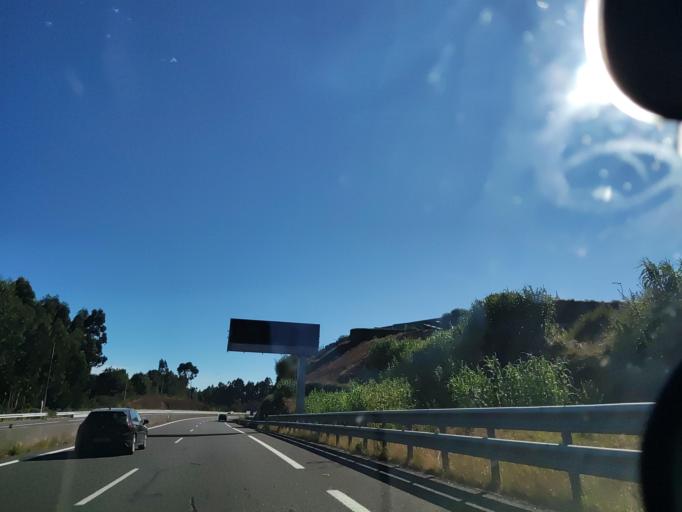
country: ES
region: Galicia
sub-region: Provincia da Coruna
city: Boiro
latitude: 42.6308
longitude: -8.9184
